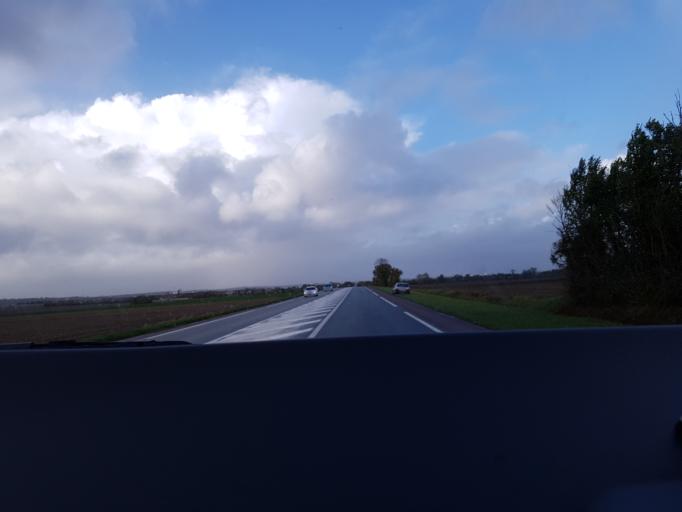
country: FR
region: Poitou-Charentes
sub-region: Departement de la Charente-Maritime
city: Les Gonds
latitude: 45.6853
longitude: -0.6114
